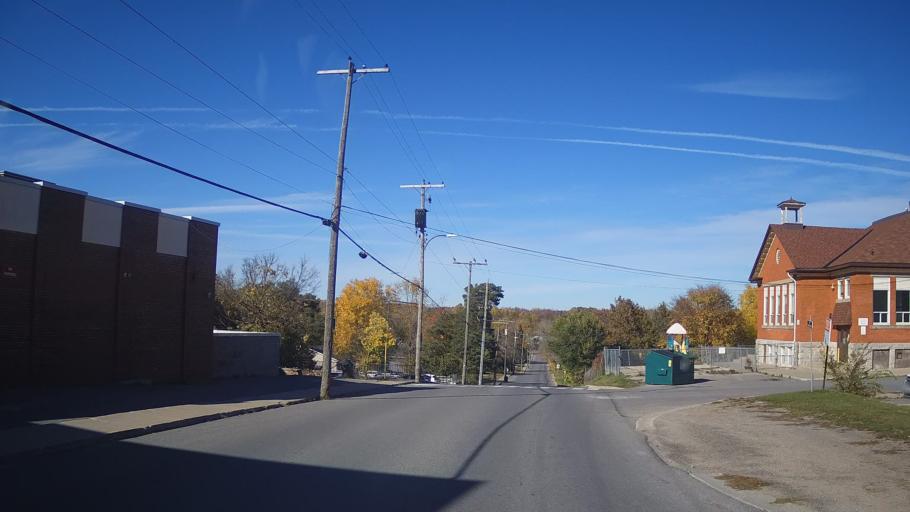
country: CA
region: Ontario
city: Kingston
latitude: 44.4075
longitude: -76.5944
